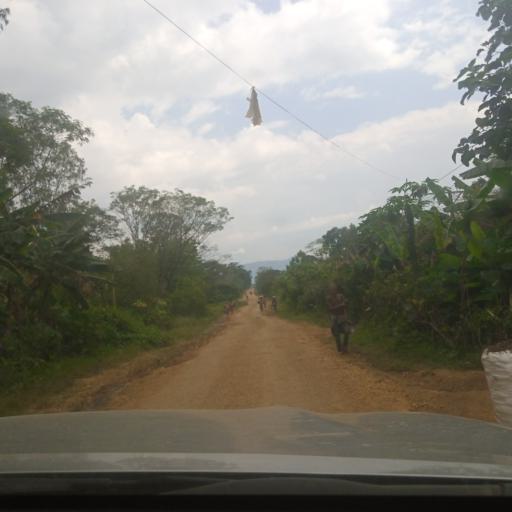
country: ET
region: Southern Nations, Nationalities, and People's Region
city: Tippi
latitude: 7.1378
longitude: 35.4218
